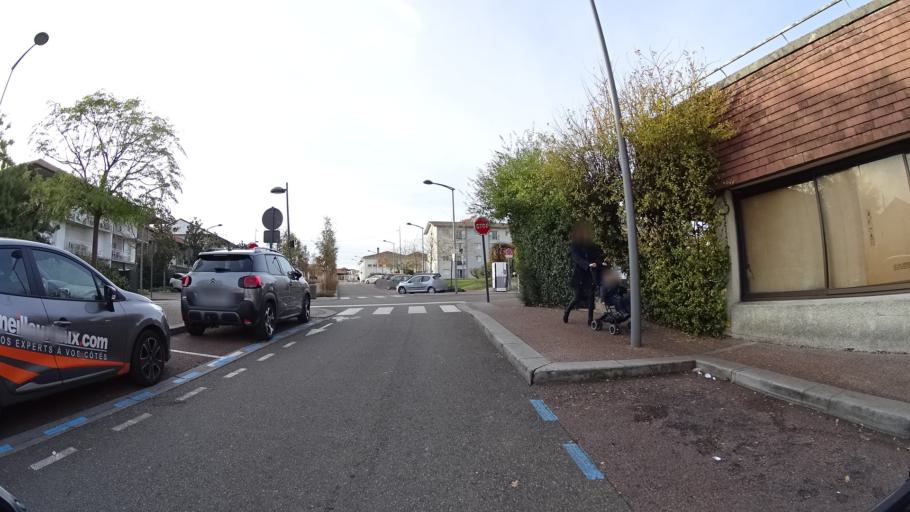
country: FR
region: Aquitaine
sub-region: Departement des Landes
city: Saint-Paul-les-Dax
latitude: 43.7229
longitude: -1.0519
